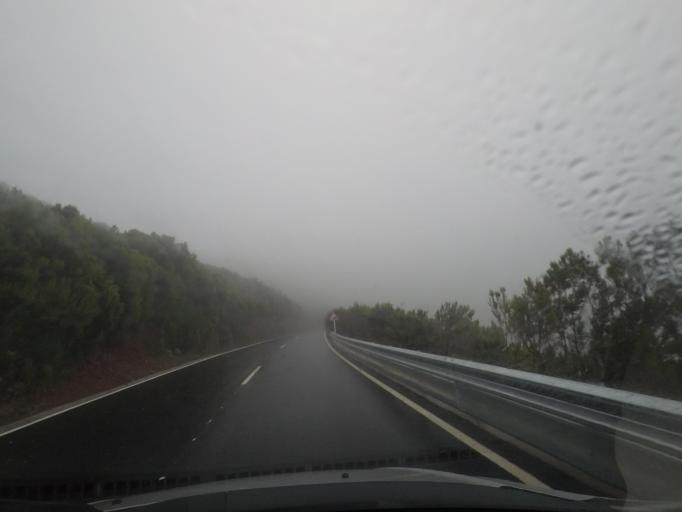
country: PT
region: Madeira
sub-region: Santana
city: Santana
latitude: 32.7660
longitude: -16.9220
